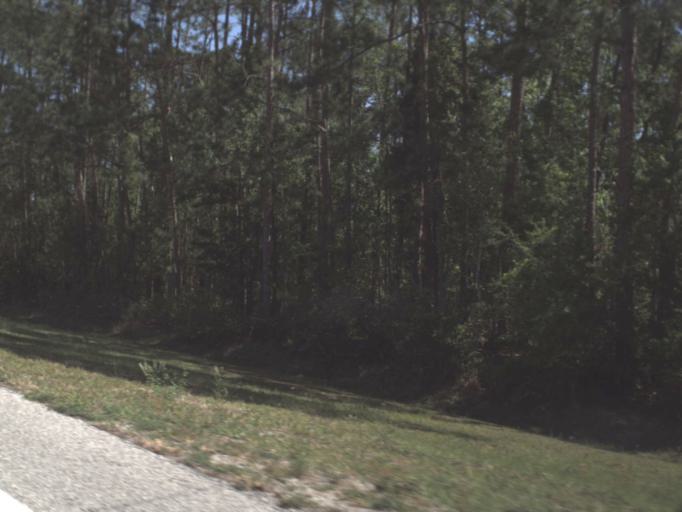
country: US
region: Florida
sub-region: Flagler County
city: Palm Coast
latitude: 29.5486
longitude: -81.2637
